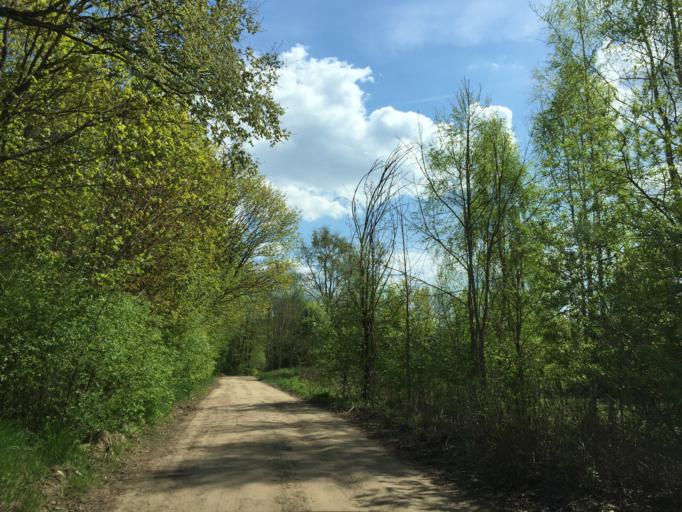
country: LV
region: Limbazu Rajons
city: Limbazi
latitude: 57.3518
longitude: 24.6609
